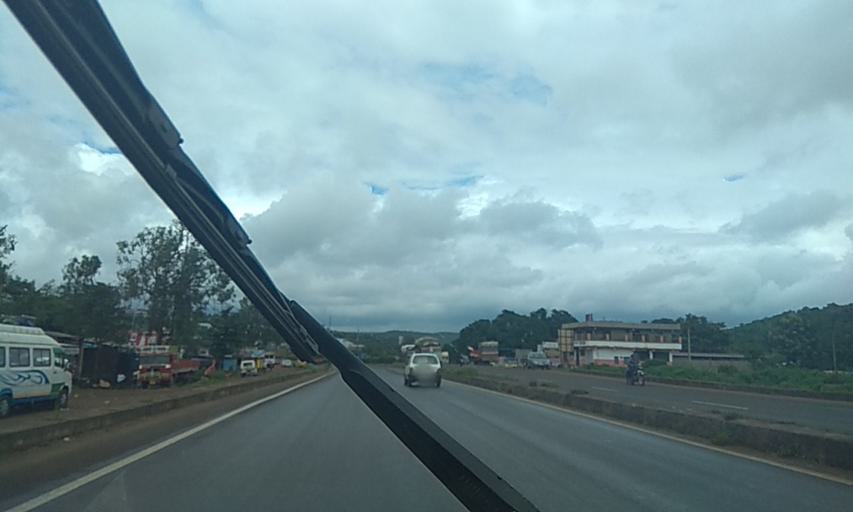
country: IN
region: Karnataka
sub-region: Belgaum
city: Belgaum
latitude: 15.9413
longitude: 74.5250
